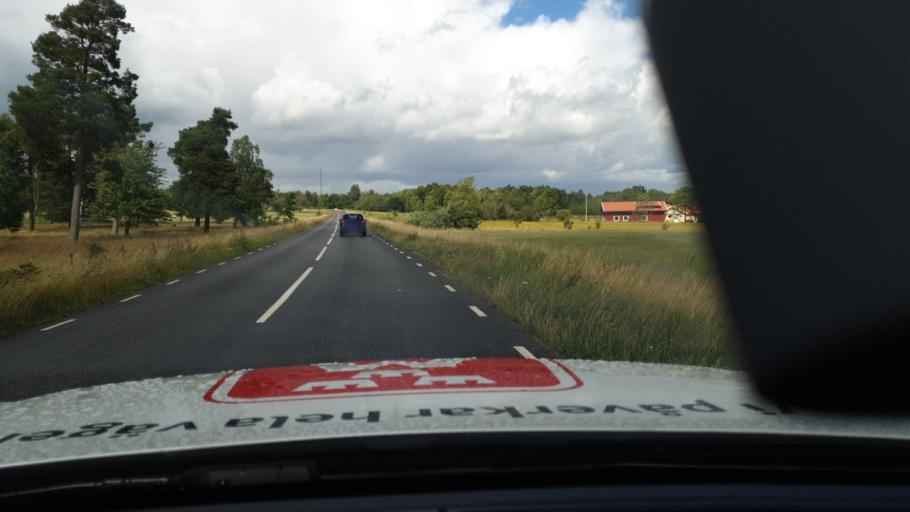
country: SE
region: Vaestra Goetaland
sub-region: Falkopings Kommun
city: Akarp
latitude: 58.1736
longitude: 13.6366
